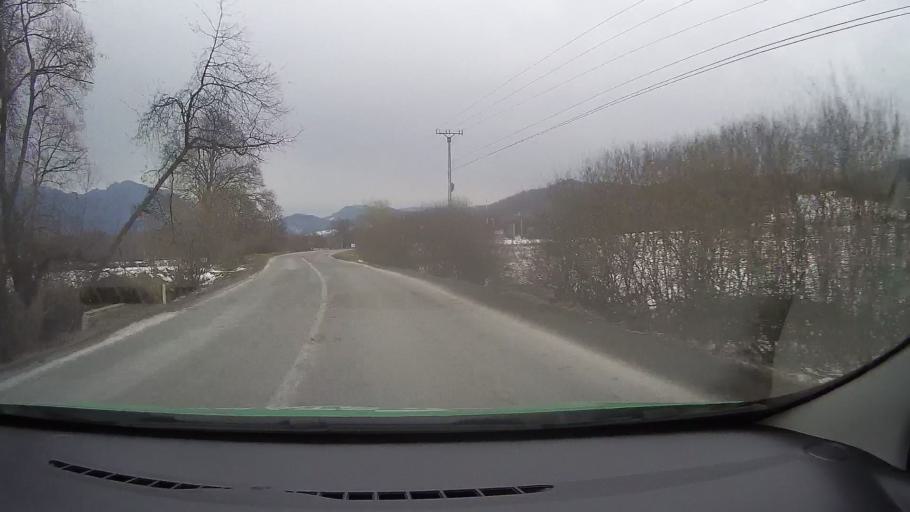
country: RO
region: Brasov
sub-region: Oras Rasnov
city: Rasnov
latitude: 45.5579
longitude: 25.4707
